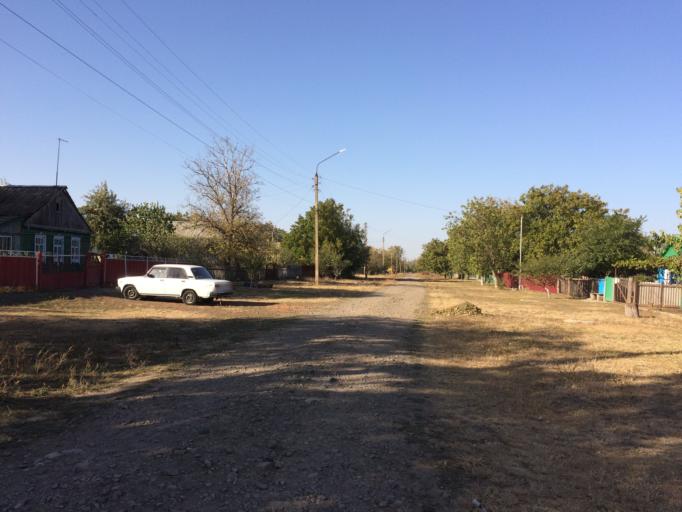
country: RU
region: Rostov
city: Gigant
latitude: 46.5206
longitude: 41.1882
